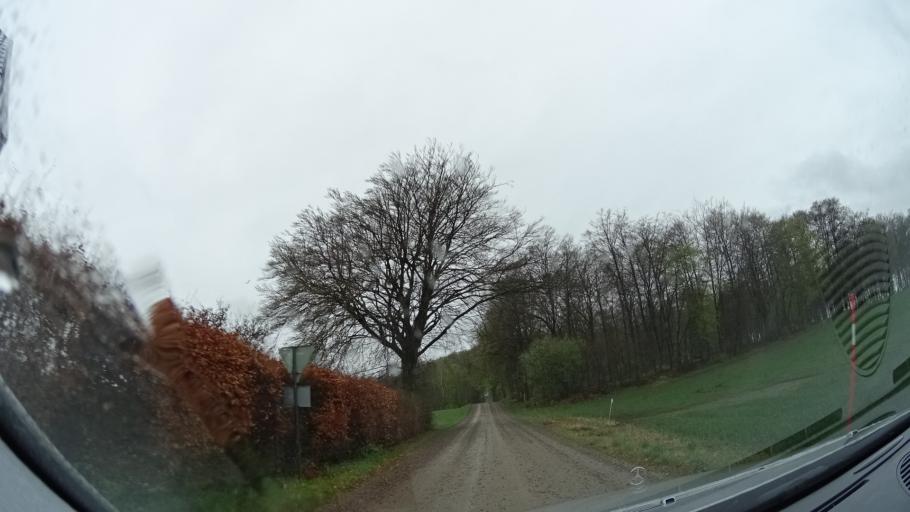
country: SE
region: Skane
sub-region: Hoors Kommun
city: Loberod
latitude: 55.8182
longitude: 13.4779
